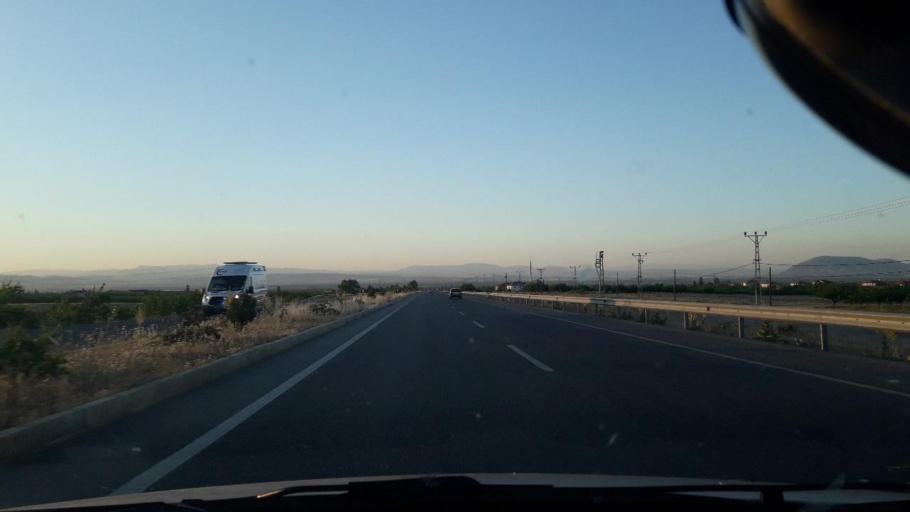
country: TR
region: Malatya
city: Malatya
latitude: 38.4255
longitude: 38.2234
